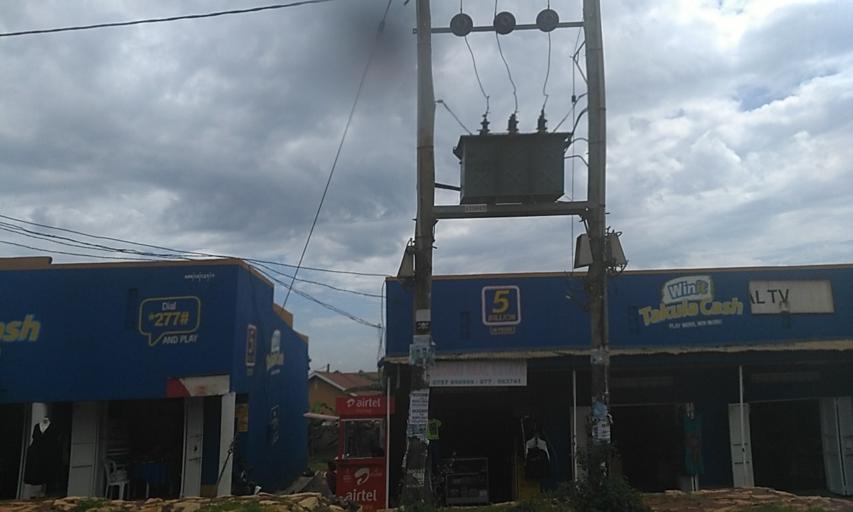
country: UG
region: Central Region
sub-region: Wakiso District
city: Bweyogerere
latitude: 0.3724
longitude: 32.6494
